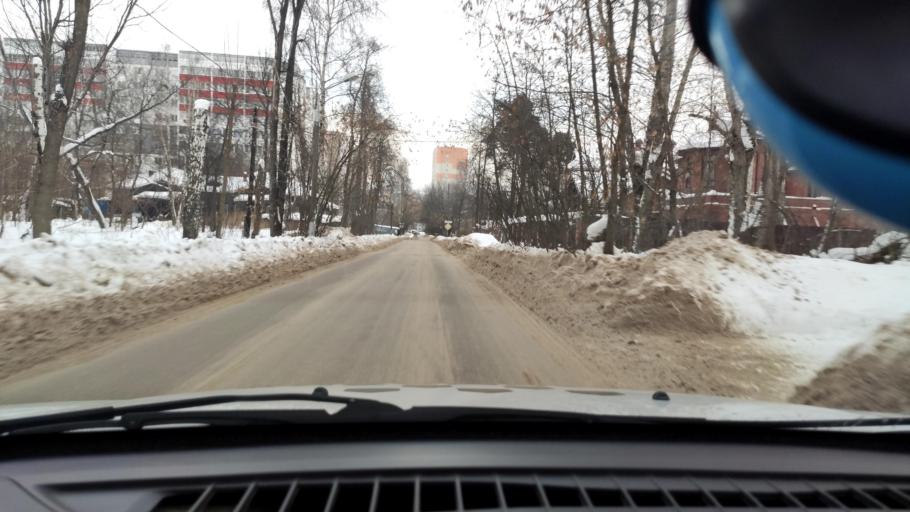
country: RU
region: Perm
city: Kondratovo
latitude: 58.0239
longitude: 56.0193
